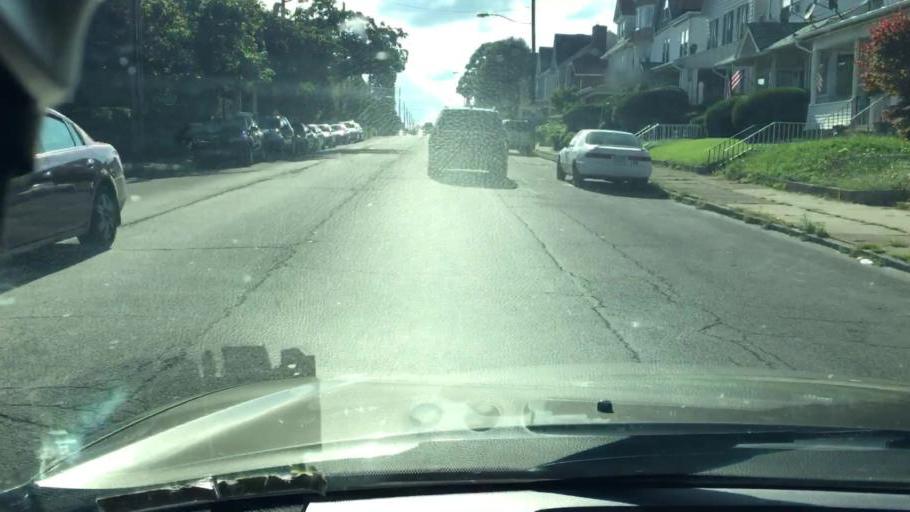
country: US
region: Pennsylvania
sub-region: Luzerne County
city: Hazleton
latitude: 40.9592
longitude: -75.9796
